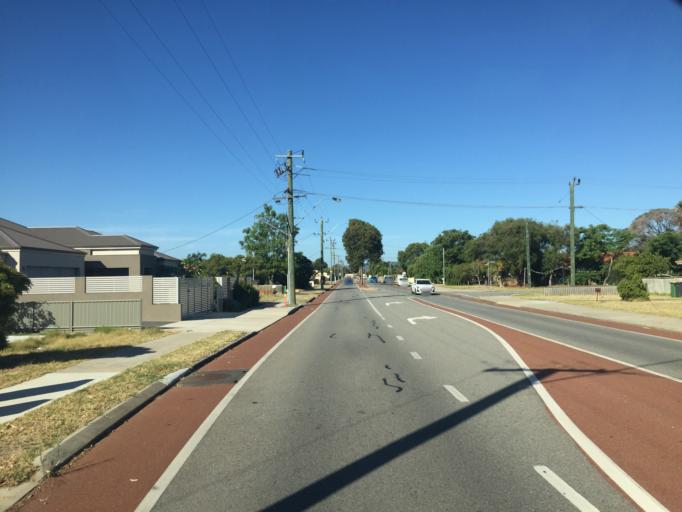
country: AU
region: Western Australia
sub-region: Canning
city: East Cannington
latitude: -32.0116
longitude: 115.9677
